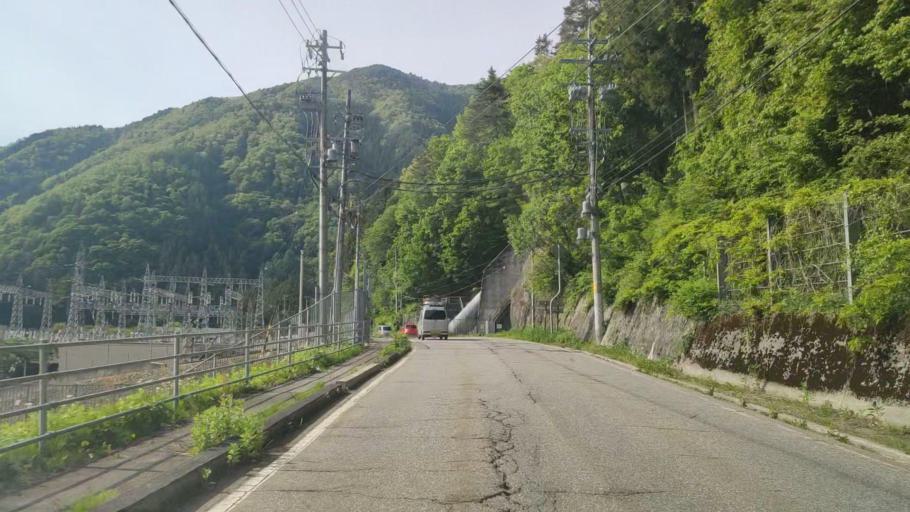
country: JP
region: Gifu
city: Takayama
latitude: 36.2935
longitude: 137.3717
